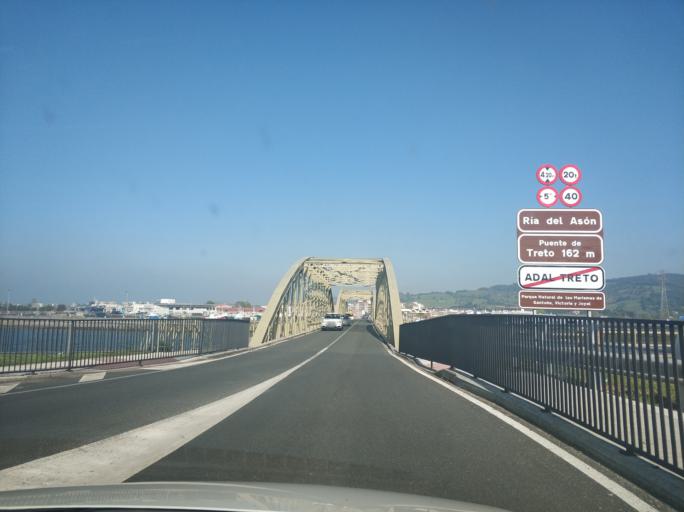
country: ES
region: Cantabria
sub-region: Provincia de Cantabria
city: Colindres
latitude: 43.3930
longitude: -3.4662
